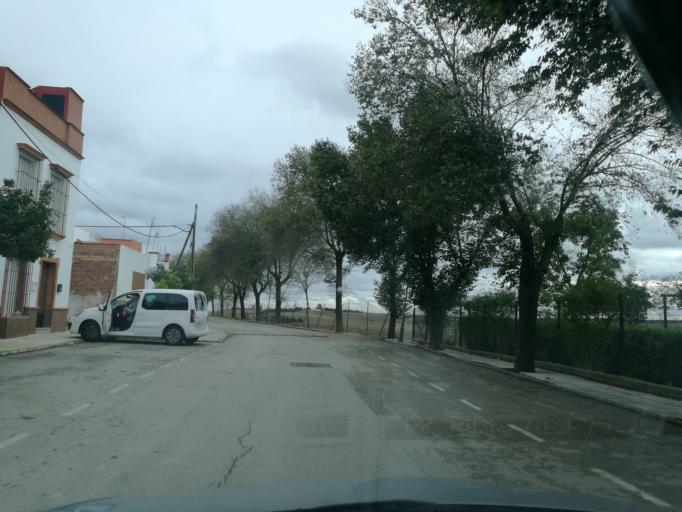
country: ES
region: Andalusia
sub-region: Provincia de Sevilla
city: La Campana
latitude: 37.5651
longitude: -5.4305
